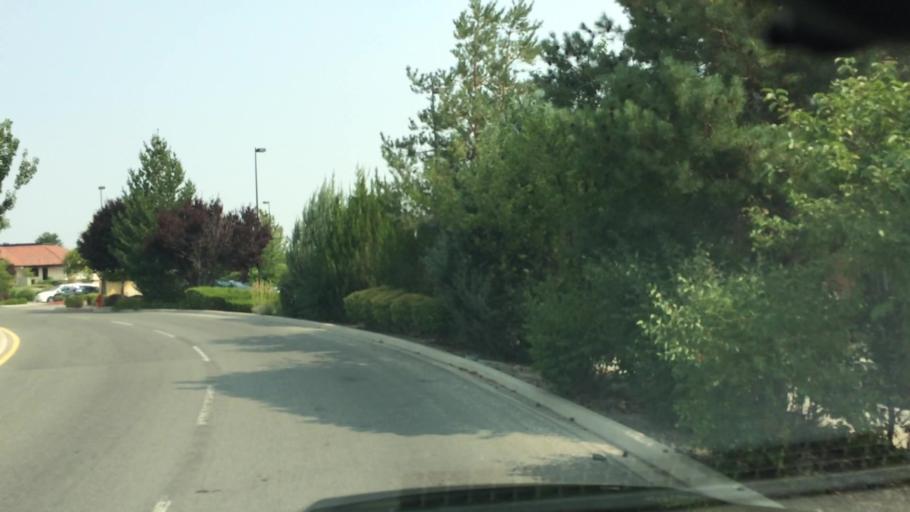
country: US
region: Nevada
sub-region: Washoe County
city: Reno
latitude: 39.4654
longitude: -119.7901
